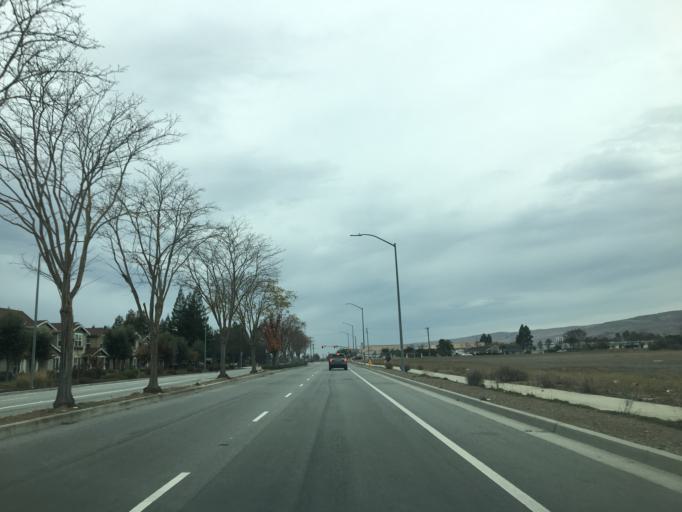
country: US
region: California
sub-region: Santa Clara County
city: Morgan Hill
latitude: 37.1456
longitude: -121.6591
